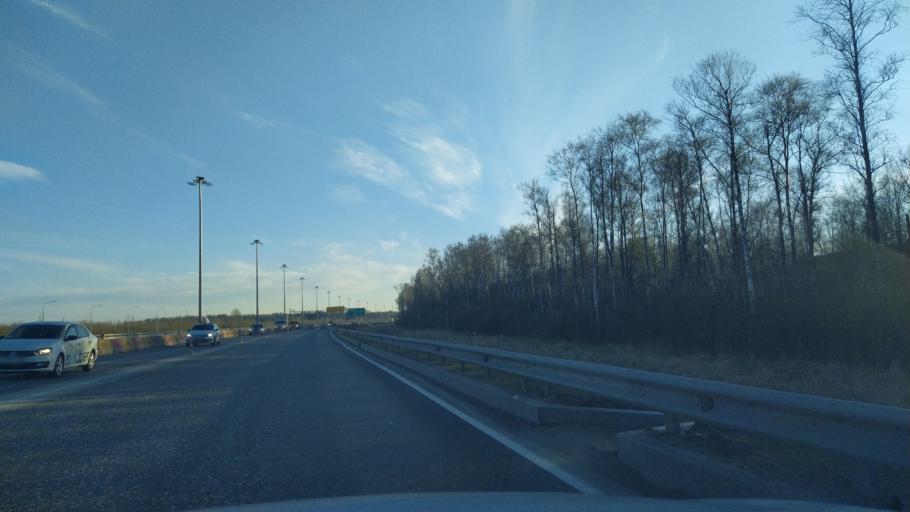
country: RU
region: St.-Petersburg
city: Levashovo
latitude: 60.0696
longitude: 30.1732
